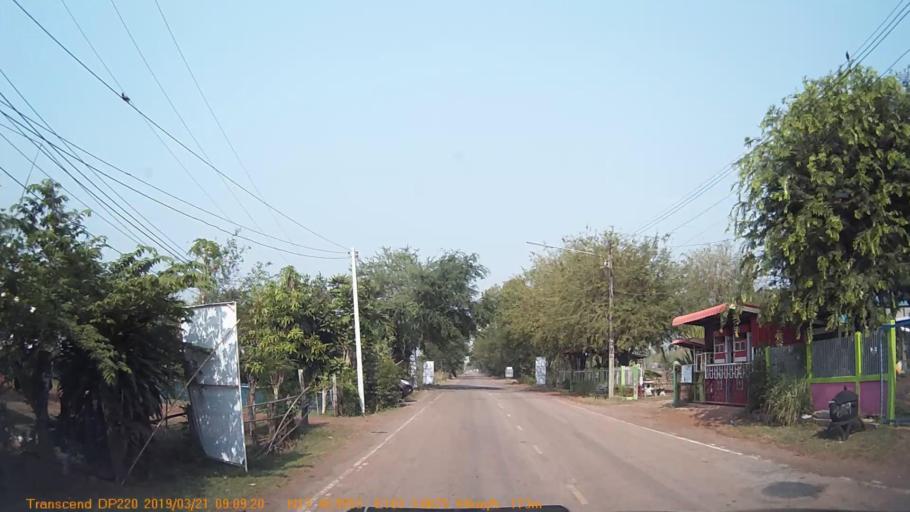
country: TH
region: Changwat Udon Thani
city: Phibun Rak
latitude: 17.6826
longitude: 103.0508
